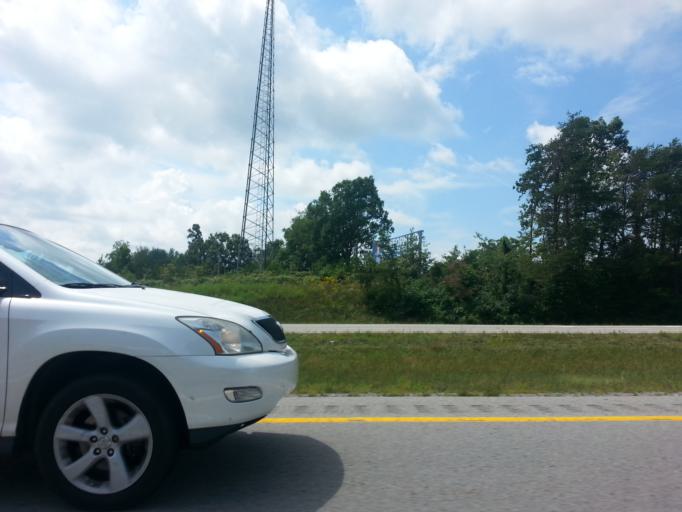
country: US
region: Tennessee
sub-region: Cumberland County
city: Crossville
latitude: 35.9605
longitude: -84.9796
